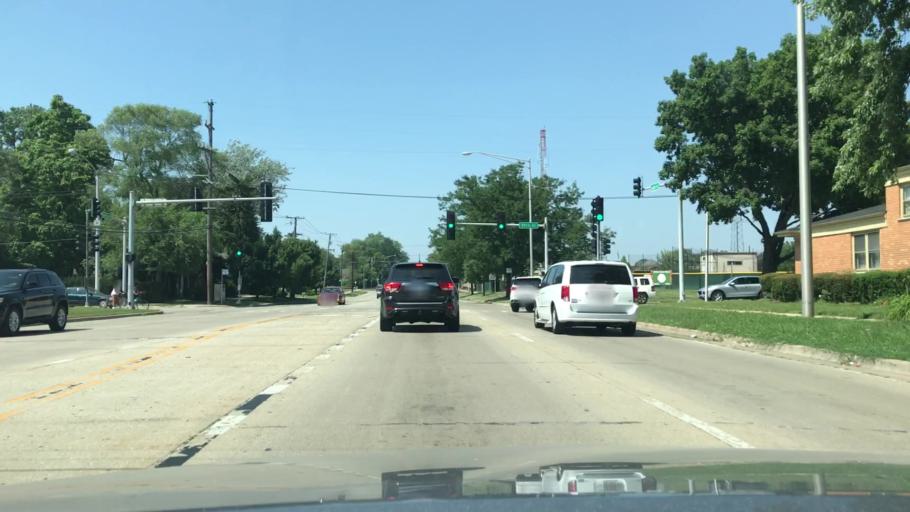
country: US
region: Illinois
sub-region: Cook County
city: Oak Lawn
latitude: 41.7120
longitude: -87.7600
